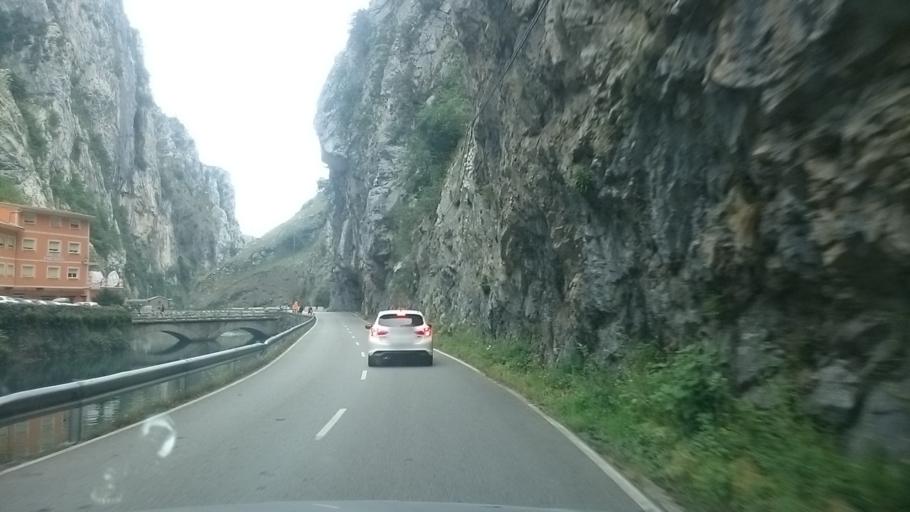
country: ES
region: Asturias
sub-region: Province of Asturias
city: Carrena
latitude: 43.2612
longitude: -4.8308
